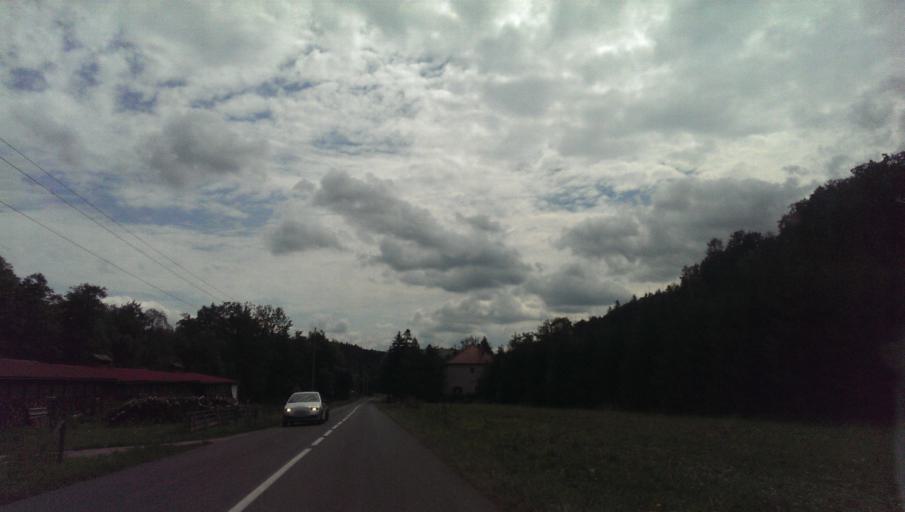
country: CZ
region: South Moravian
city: Velka nad Velickou
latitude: 48.8955
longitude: 17.5750
